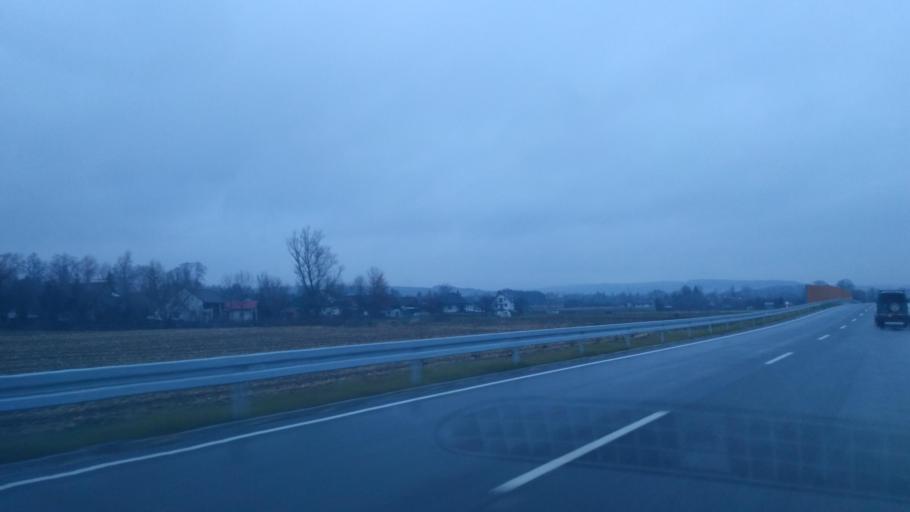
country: PL
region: Subcarpathian Voivodeship
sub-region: Powiat rzeszowski
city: Dynow
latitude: 49.8181
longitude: 22.2408
